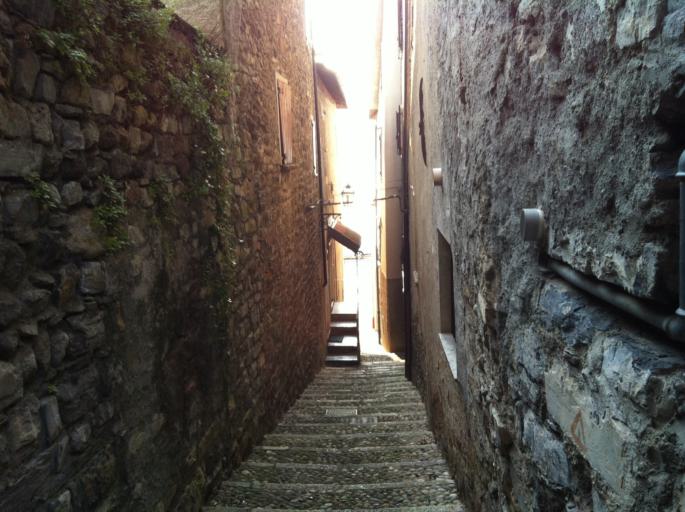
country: IT
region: Lombardy
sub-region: Provincia di Como
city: Menaggio
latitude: 46.0339
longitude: 9.2369
